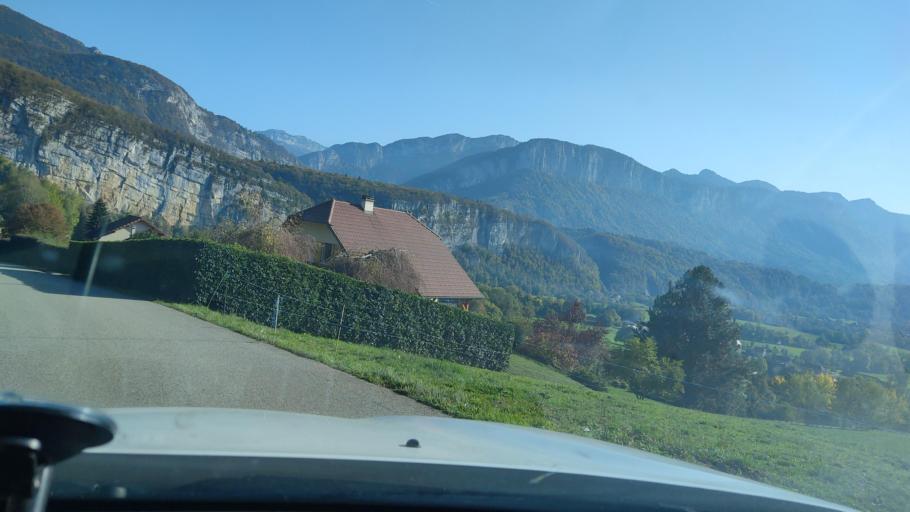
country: FR
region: Rhone-Alpes
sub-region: Departement de la Savoie
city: Les Echelles
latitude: 45.4574
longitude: 5.7773
